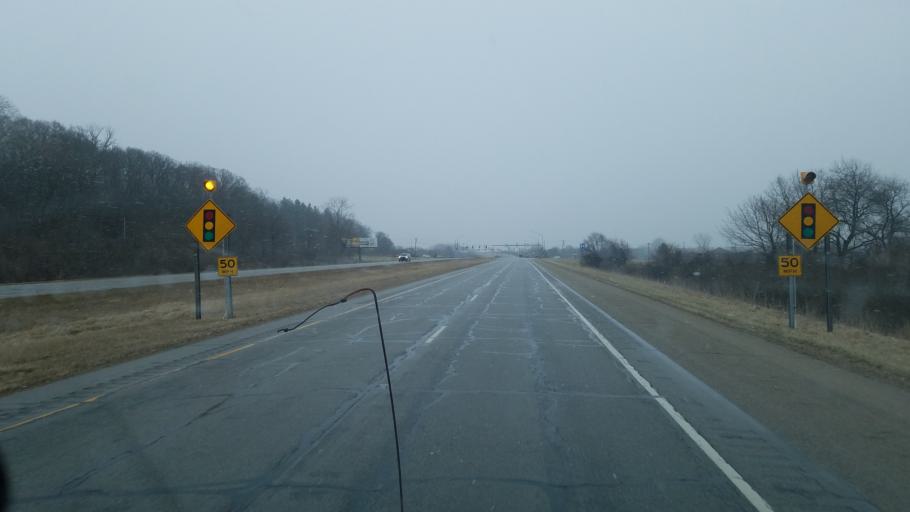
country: US
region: Indiana
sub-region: Miami County
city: Peru
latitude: 40.7730
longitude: -86.0872
